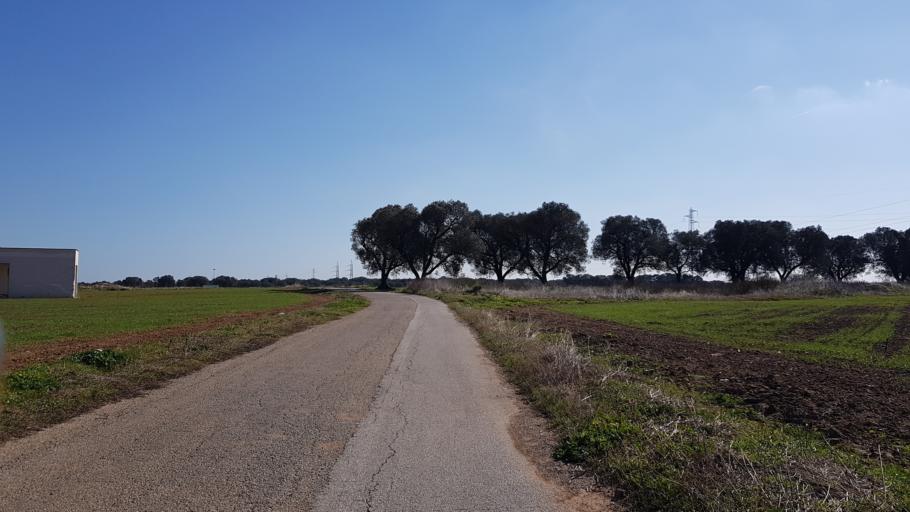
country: IT
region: Apulia
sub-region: Provincia di Brindisi
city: Mesagne
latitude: 40.6206
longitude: 17.8292
